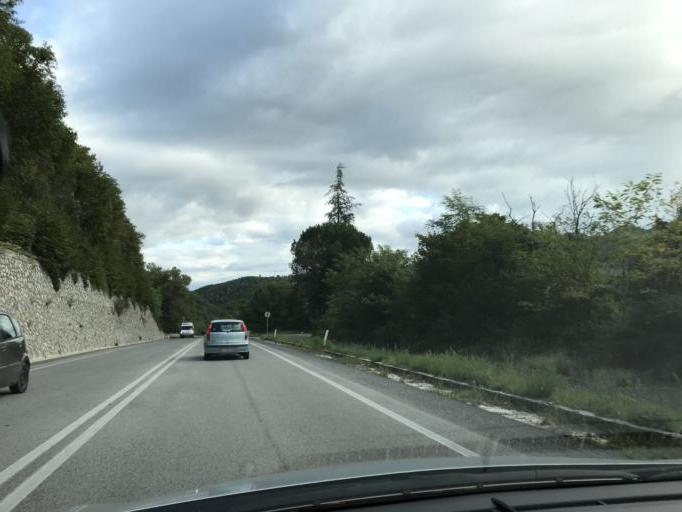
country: IT
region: Umbria
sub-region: Provincia di Perugia
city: Spoleto
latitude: 42.6926
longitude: 12.7214
